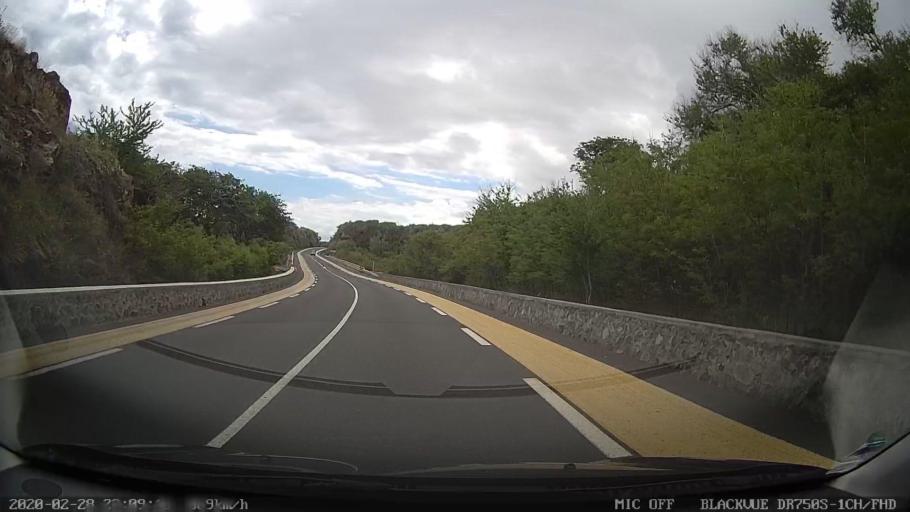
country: RE
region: Reunion
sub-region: Reunion
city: Trois-Bassins
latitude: -21.1268
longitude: 55.2688
